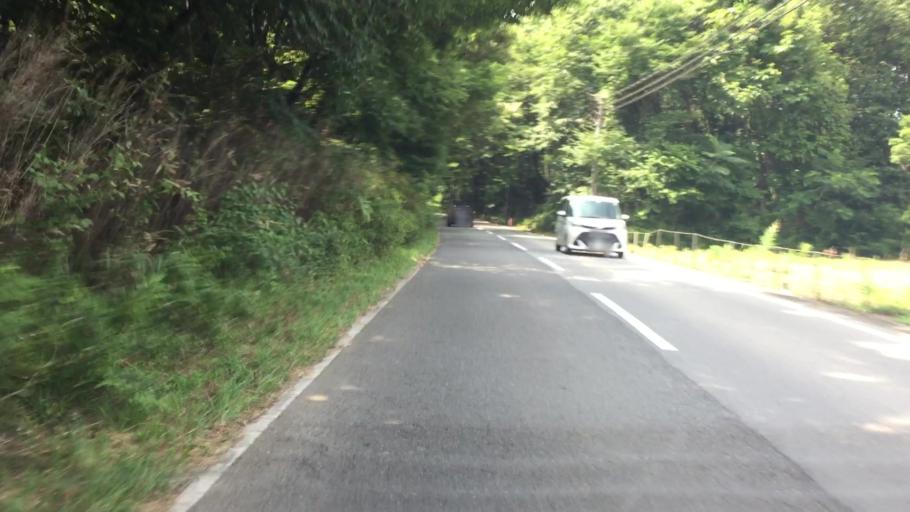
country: JP
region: Tochigi
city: Kuroiso
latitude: 36.9468
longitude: 139.9603
